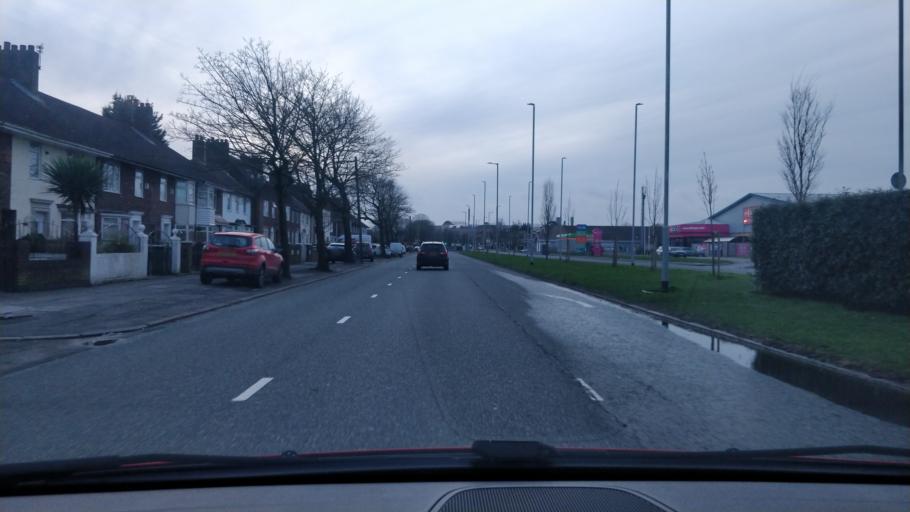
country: GB
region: England
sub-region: Knowsley
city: Huyton
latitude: 53.4194
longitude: -2.8828
